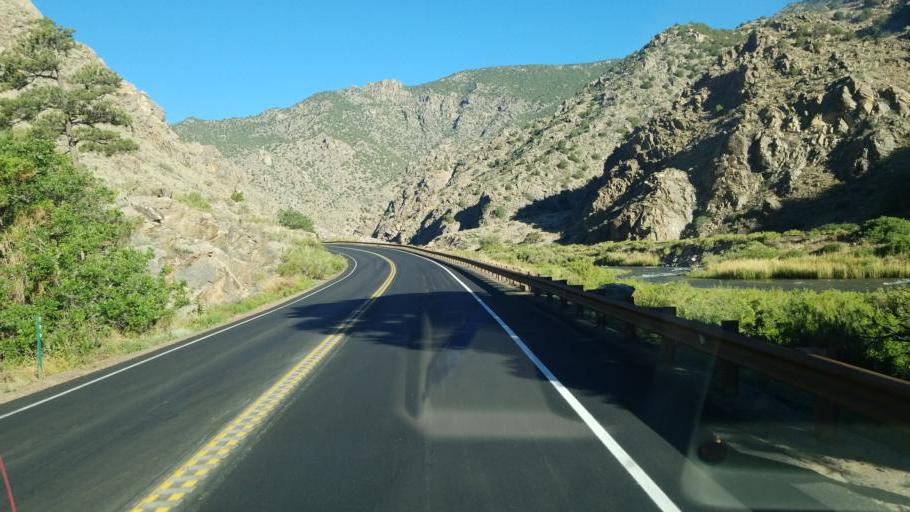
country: US
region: Colorado
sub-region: Fremont County
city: Canon City
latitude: 38.4552
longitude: -105.5009
